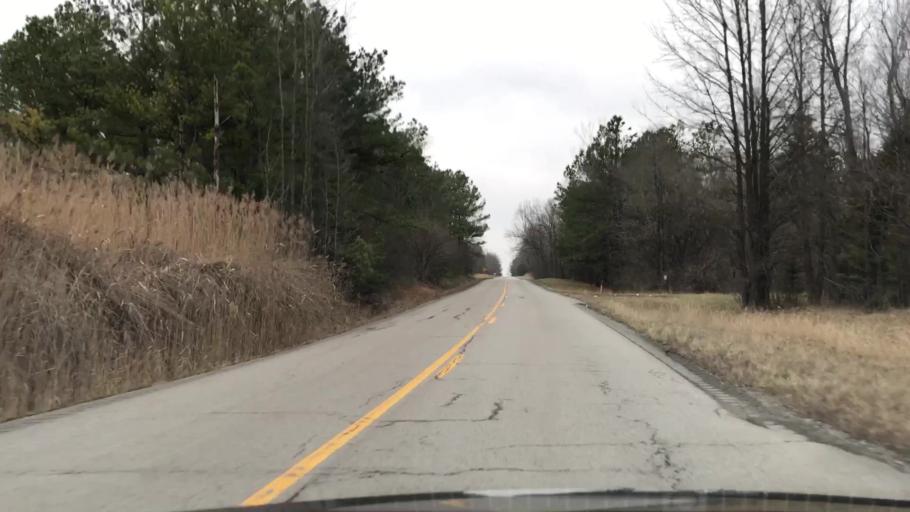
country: US
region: Kentucky
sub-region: Muhlenberg County
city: Morehead
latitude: 37.2778
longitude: -87.2084
